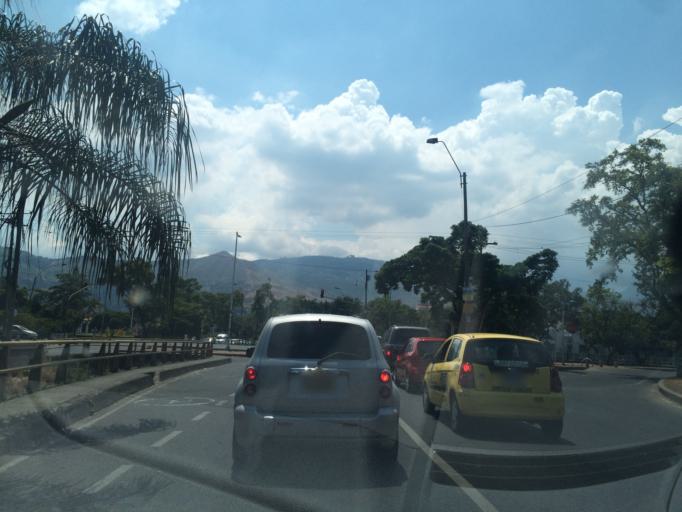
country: CO
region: Valle del Cauca
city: Cali
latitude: 3.4835
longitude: -76.5130
